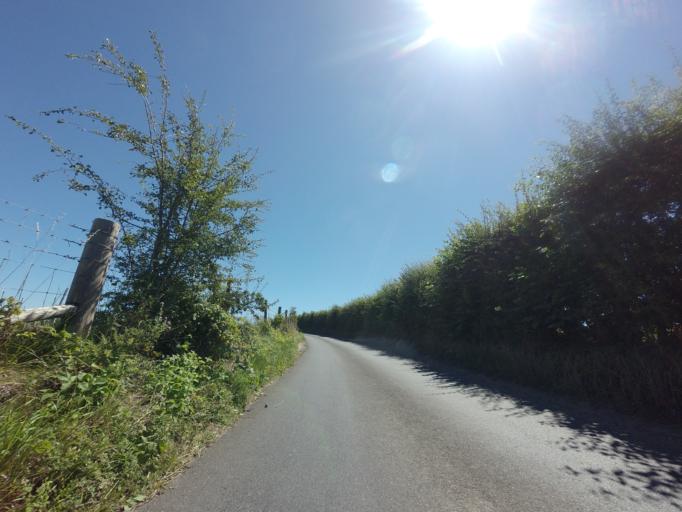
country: GB
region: England
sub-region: Kent
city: Eastry
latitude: 51.2026
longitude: 1.3081
